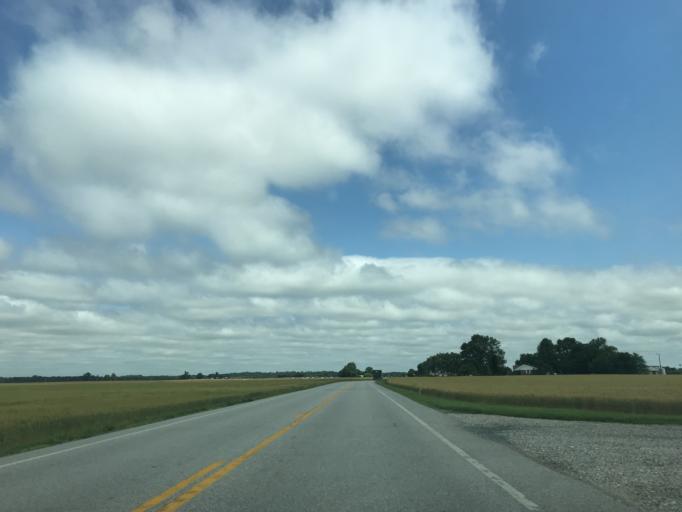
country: US
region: Maryland
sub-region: Caroline County
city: Ridgely
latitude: 38.9261
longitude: -75.8936
